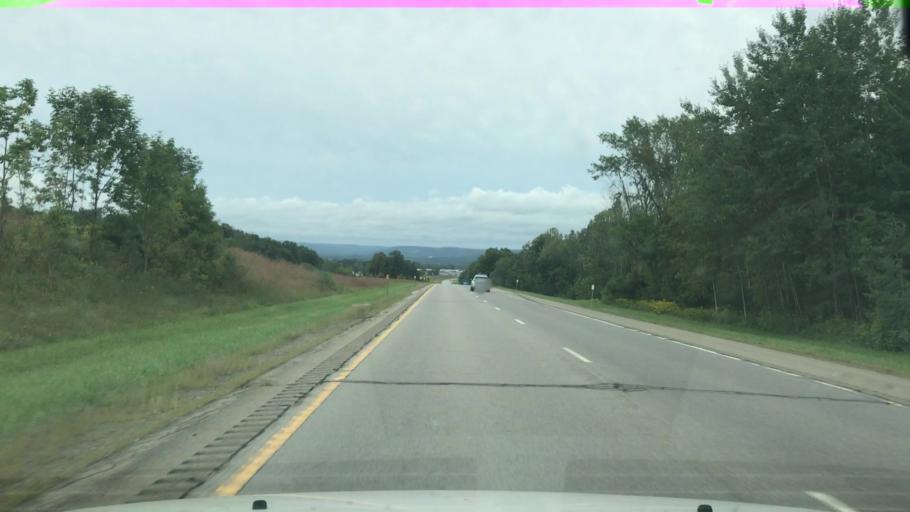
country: US
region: New York
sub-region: Erie County
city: Springville
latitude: 42.5246
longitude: -78.7001
